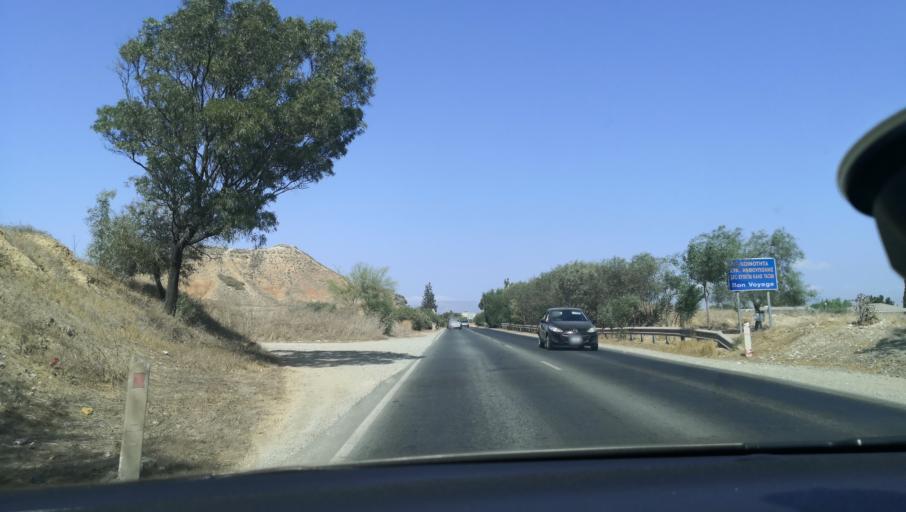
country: CY
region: Lefkosia
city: Kato Deftera
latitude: 35.1061
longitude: 33.2857
